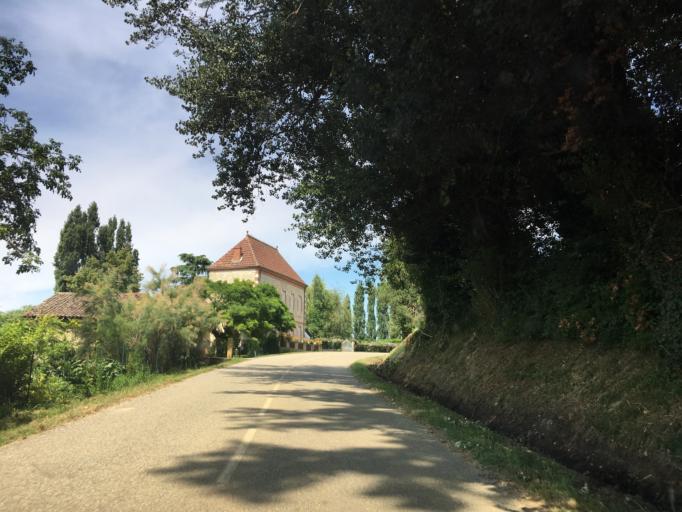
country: FR
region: Midi-Pyrenees
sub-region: Departement du Tarn-et-Garonne
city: Auvillar
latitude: 44.0440
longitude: 0.8552
